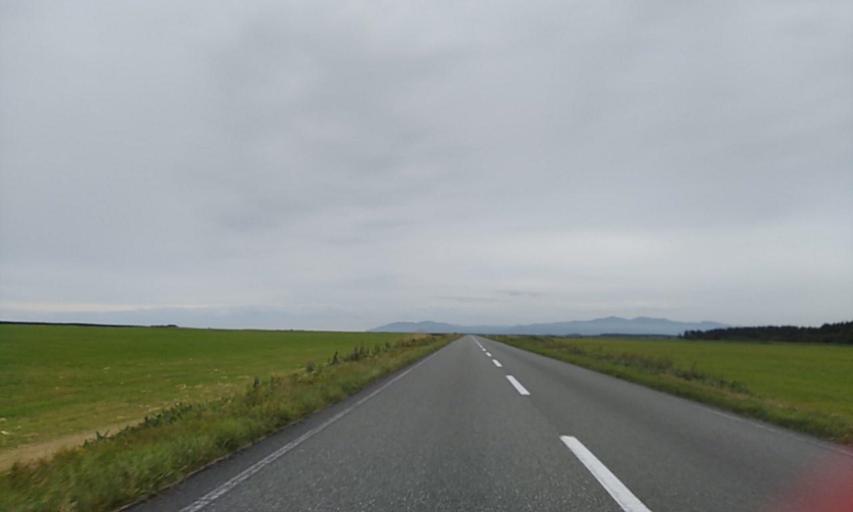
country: JP
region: Hokkaido
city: Makubetsu
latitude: 45.2146
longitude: 142.2854
